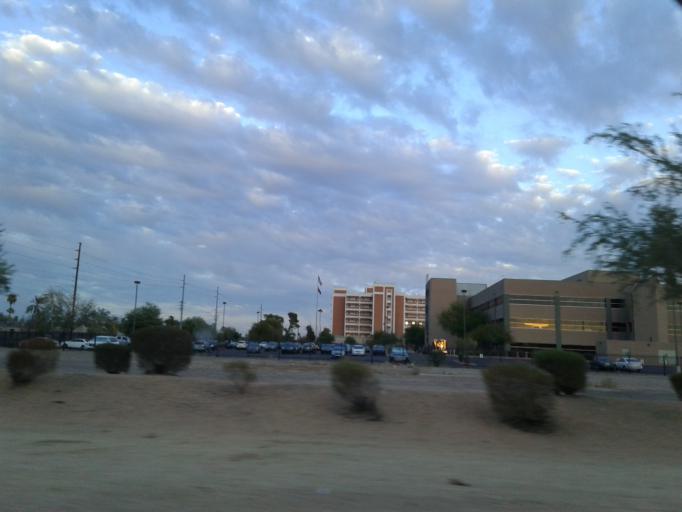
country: US
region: Arizona
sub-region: Maricopa County
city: Phoenix
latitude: 33.4578
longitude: -112.0301
